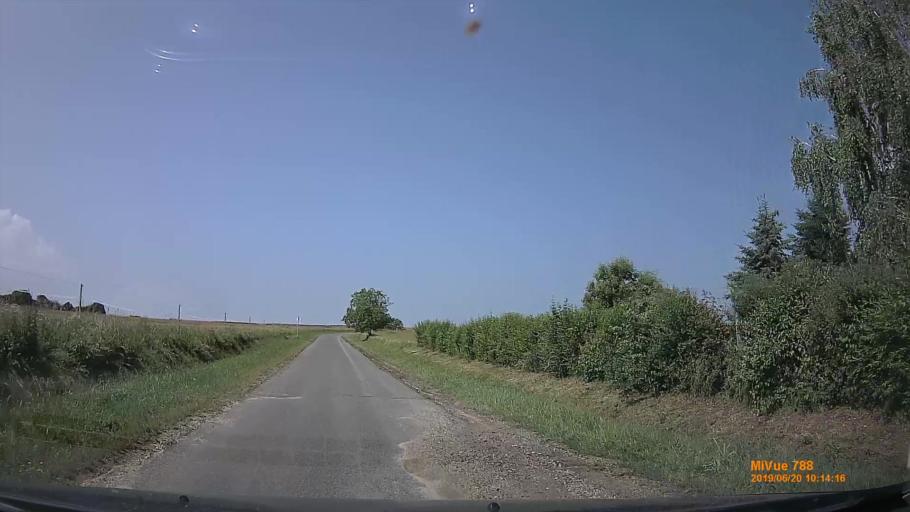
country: HU
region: Baranya
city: Mecseknadasd
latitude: 46.1903
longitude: 18.4752
